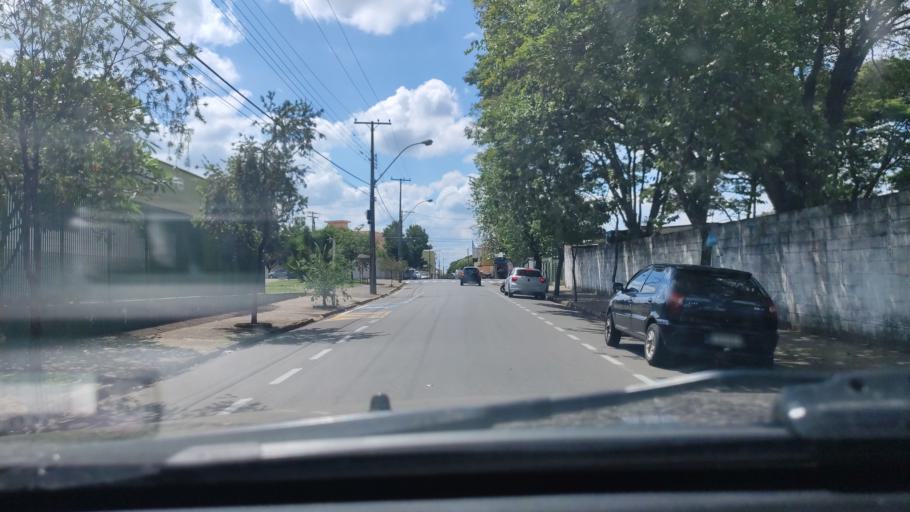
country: BR
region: Sao Paulo
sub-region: Sao Carlos
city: Sao Carlos
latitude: -22.0007
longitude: -47.8794
